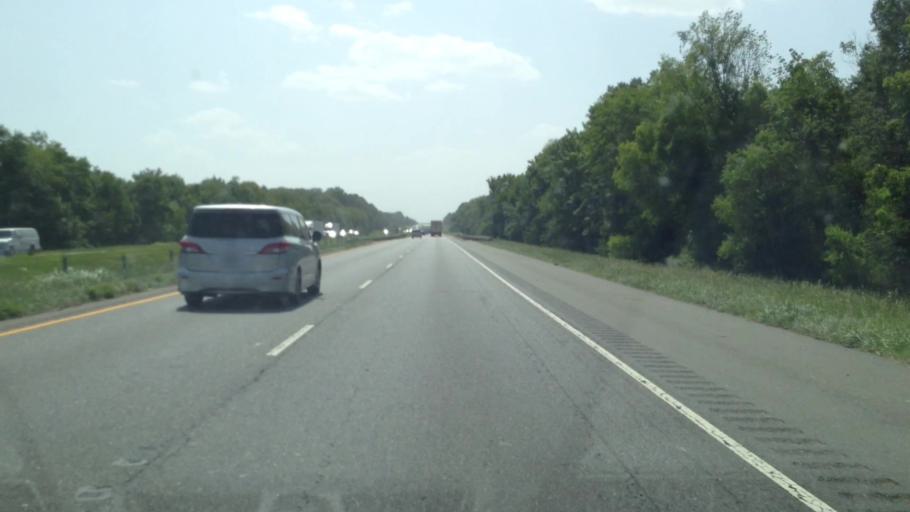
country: US
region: Louisiana
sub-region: Bossier Parish
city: Eastwood
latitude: 32.5421
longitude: -93.5795
